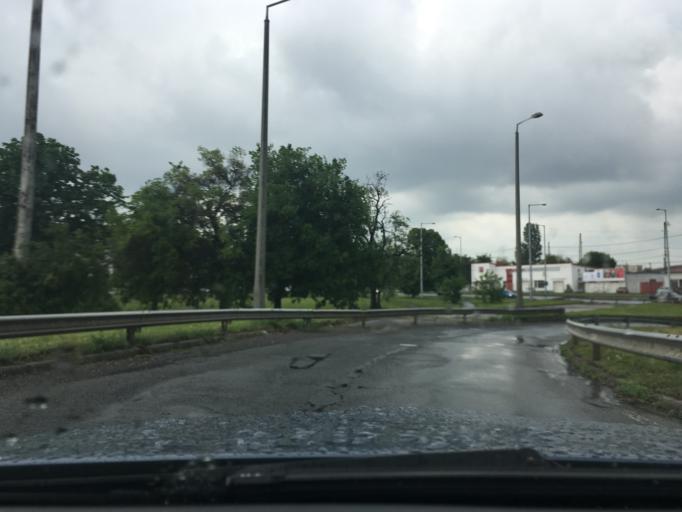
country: HU
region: Hajdu-Bihar
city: Debrecen
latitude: 47.5225
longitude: 21.6328
